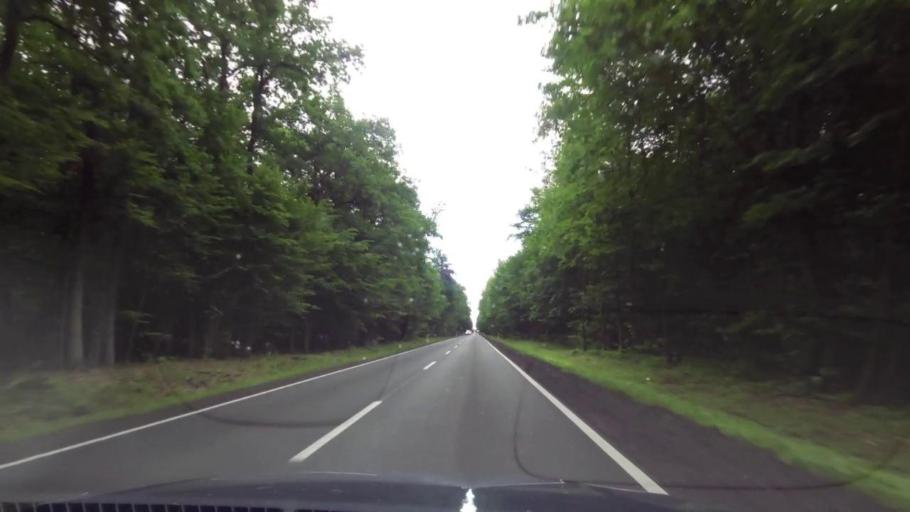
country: PL
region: West Pomeranian Voivodeship
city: Trzcinsko Zdroj
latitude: 52.9715
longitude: 14.7350
